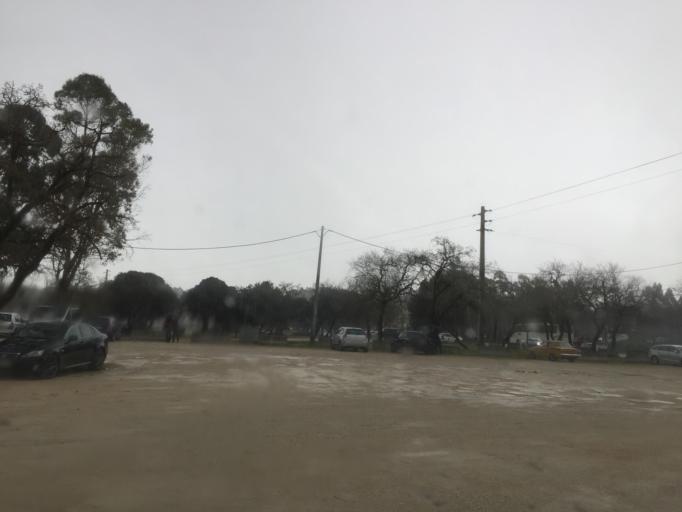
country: PT
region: Santarem
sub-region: Ourem
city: Fatima
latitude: 39.6263
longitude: -8.6776
